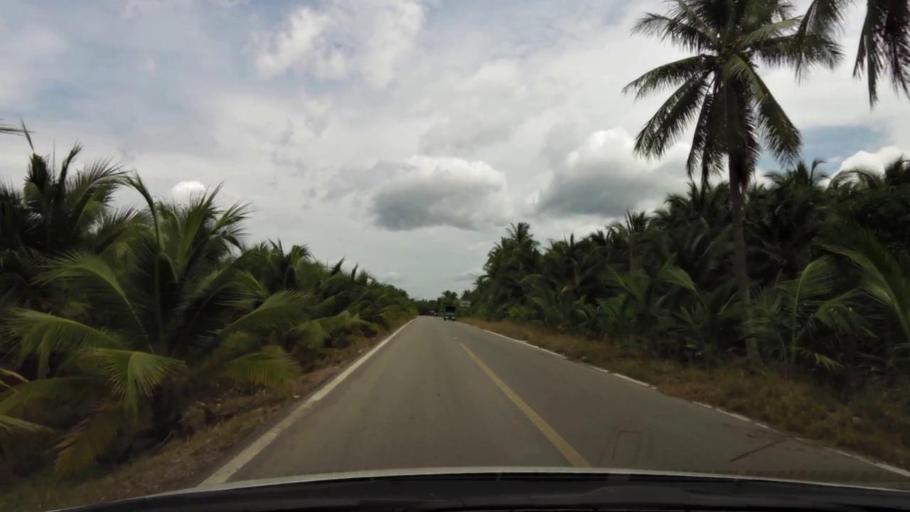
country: TH
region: Ratchaburi
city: Damnoen Saduak
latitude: 13.5219
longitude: 100.0168
